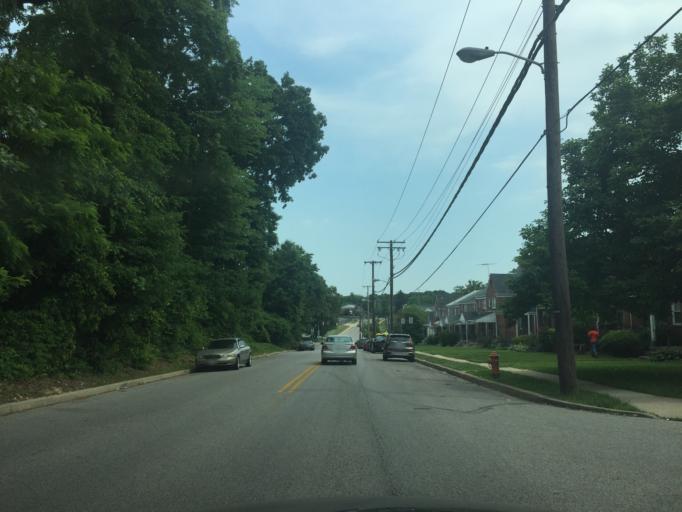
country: US
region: Maryland
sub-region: Baltimore County
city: Parkville
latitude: 39.3565
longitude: -76.5824
